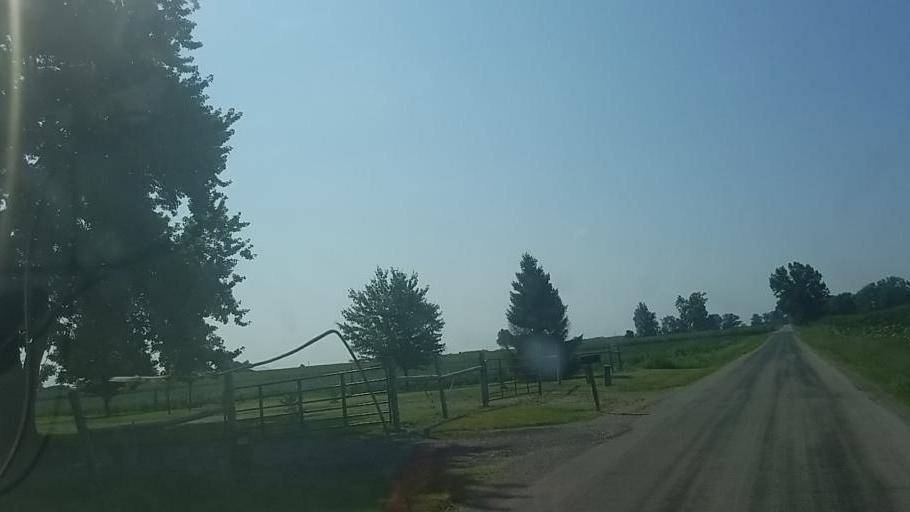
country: US
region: Ohio
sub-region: Marion County
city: Marion
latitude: 40.7042
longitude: -83.1499
